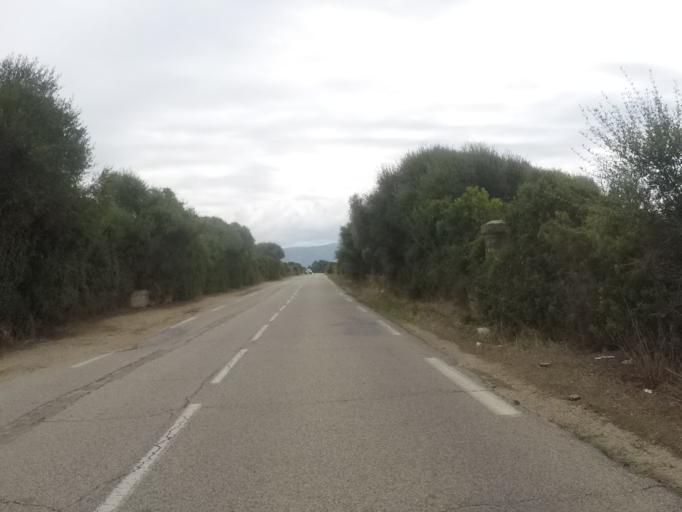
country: FR
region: Corsica
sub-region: Departement de la Corse-du-Sud
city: Propriano
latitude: 41.7080
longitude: 8.8305
